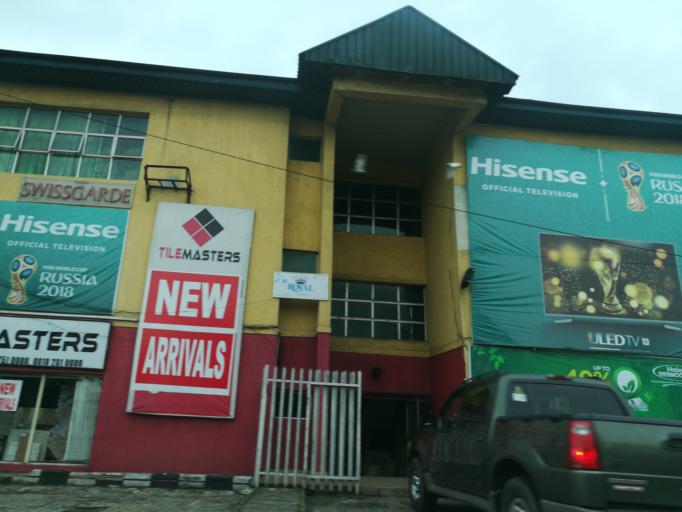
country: NG
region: Rivers
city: Port Harcourt
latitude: 4.8360
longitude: 7.0196
